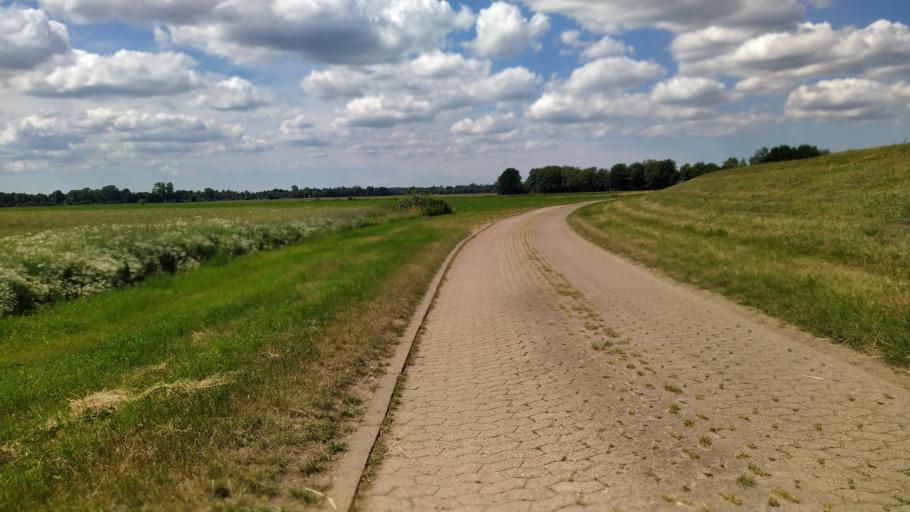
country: DE
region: Lower Saxony
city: Estorf
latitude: 53.5682
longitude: 9.1687
